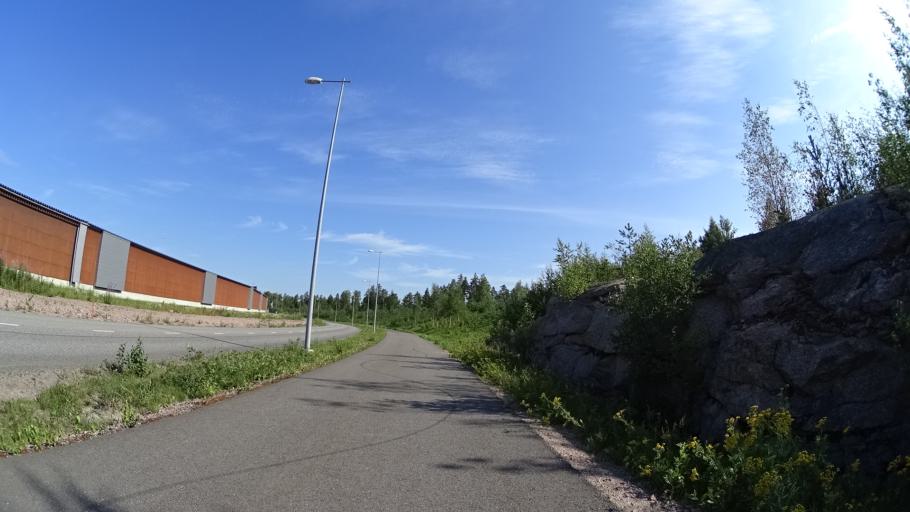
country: FI
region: Uusimaa
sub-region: Helsinki
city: Kilo
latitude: 60.2927
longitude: 24.7679
